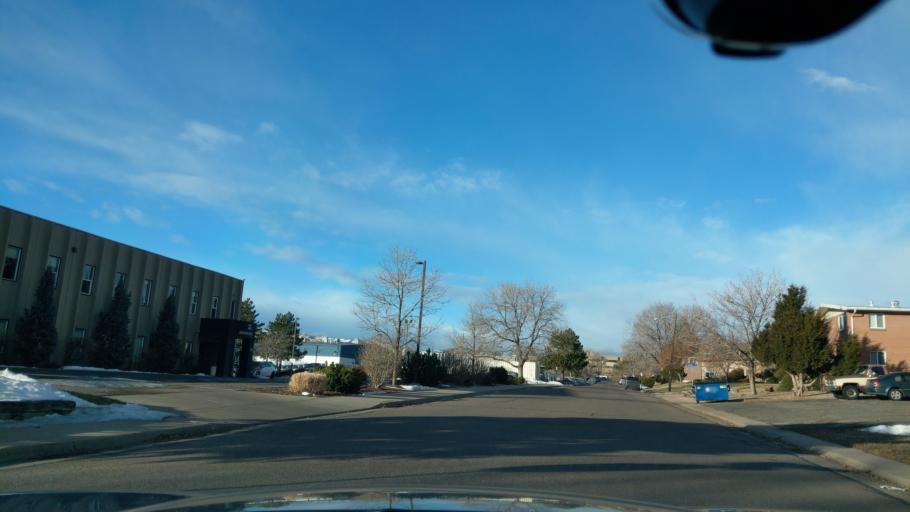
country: US
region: Colorado
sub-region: Jefferson County
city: Lakewood
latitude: 39.7271
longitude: -105.1150
